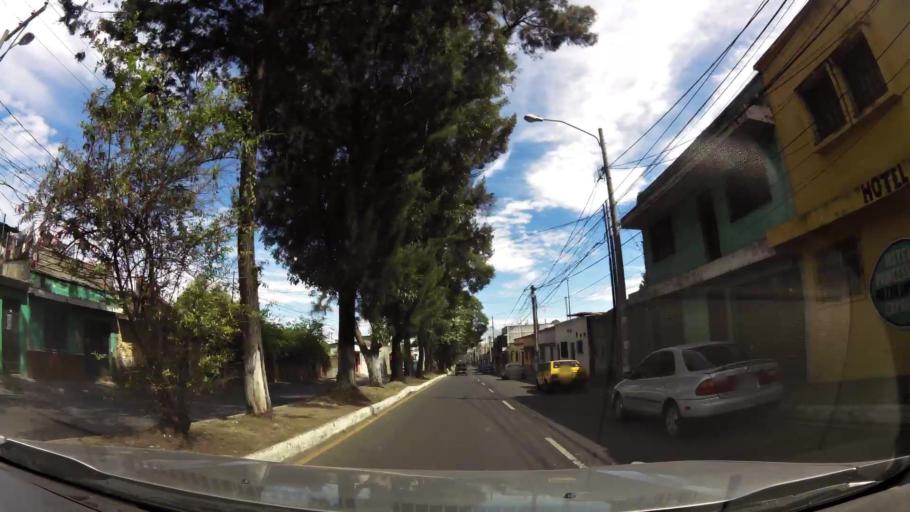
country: GT
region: Guatemala
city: Mixco
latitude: 14.6549
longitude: -90.5849
